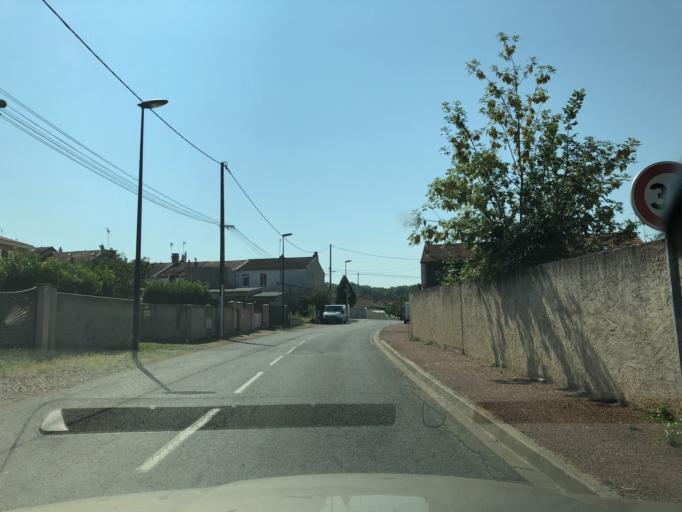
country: FR
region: Auvergne
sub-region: Departement de l'Allier
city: Cusset
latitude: 46.1319
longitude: 3.4660
